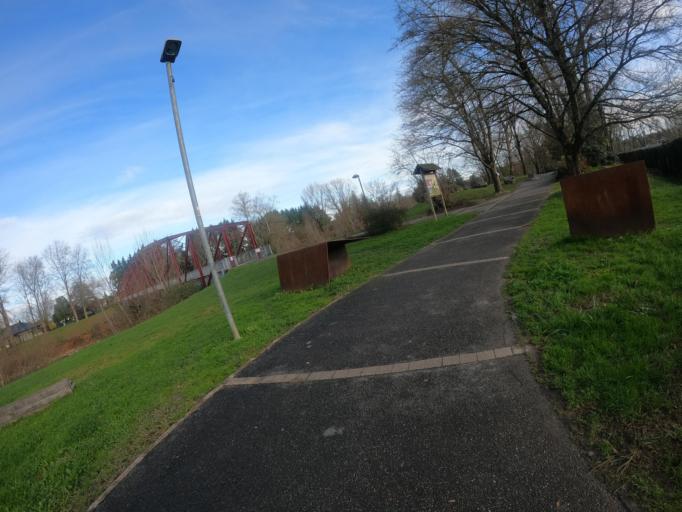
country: FR
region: Aquitaine
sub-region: Departement des Pyrenees-Atlantiques
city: Billere
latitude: 43.2937
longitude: -0.4017
